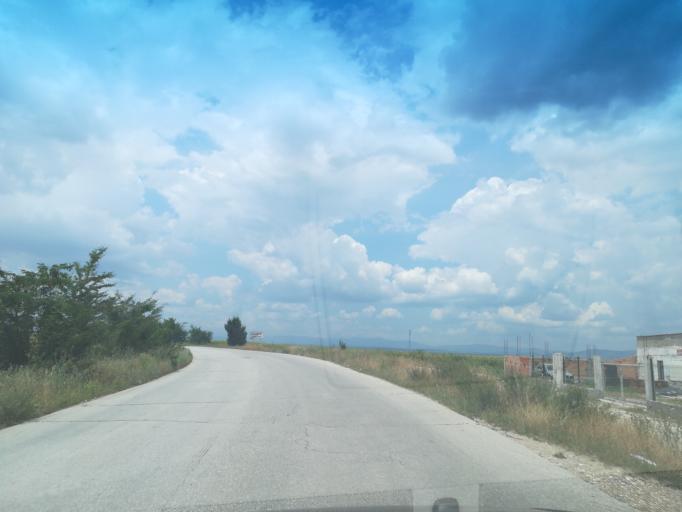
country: BG
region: Stara Zagora
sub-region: Obshtina Chirpan
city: Chirpan
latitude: 42.1811
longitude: 25.2068
